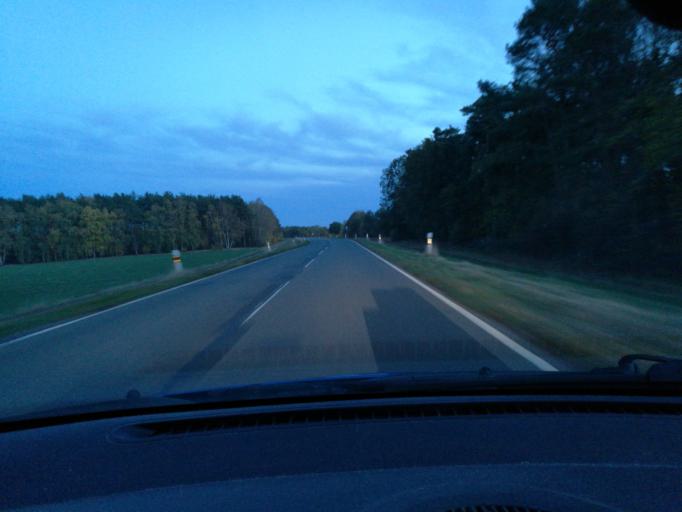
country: DE
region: Lower Saxony
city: Gartow
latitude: 53.0344
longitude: 11.4555
